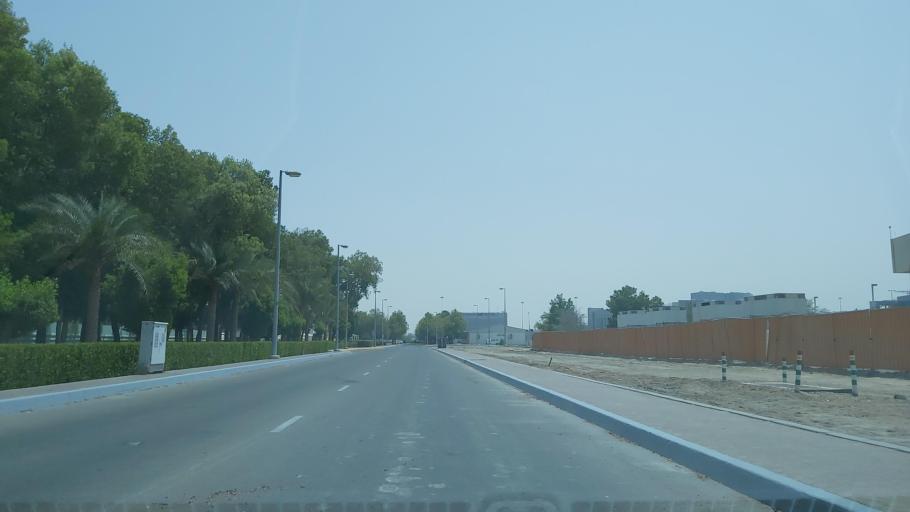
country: AE
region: Abu Dhabi
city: Abu Dhabi
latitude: 24.3793
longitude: 54.5197
